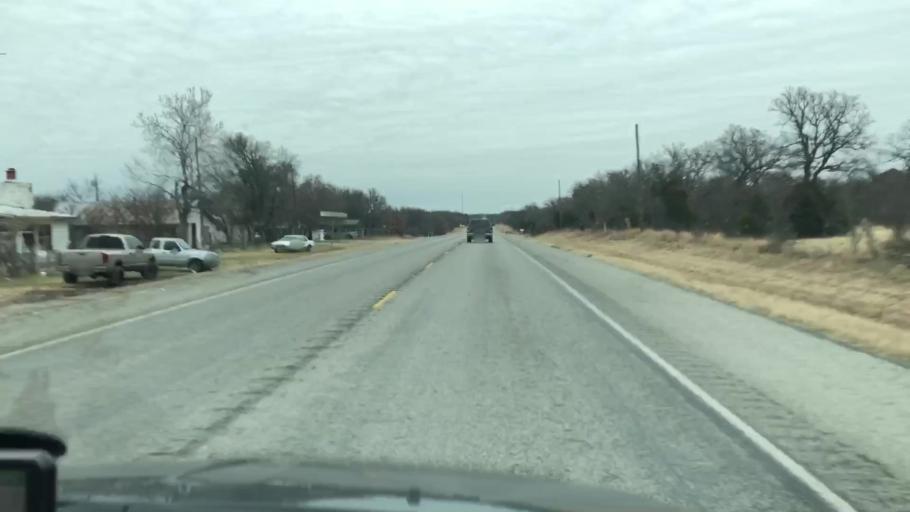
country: US
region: Texas
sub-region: Palo Pinto County
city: Mineral Wells
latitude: 32.8930
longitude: -98.0869
